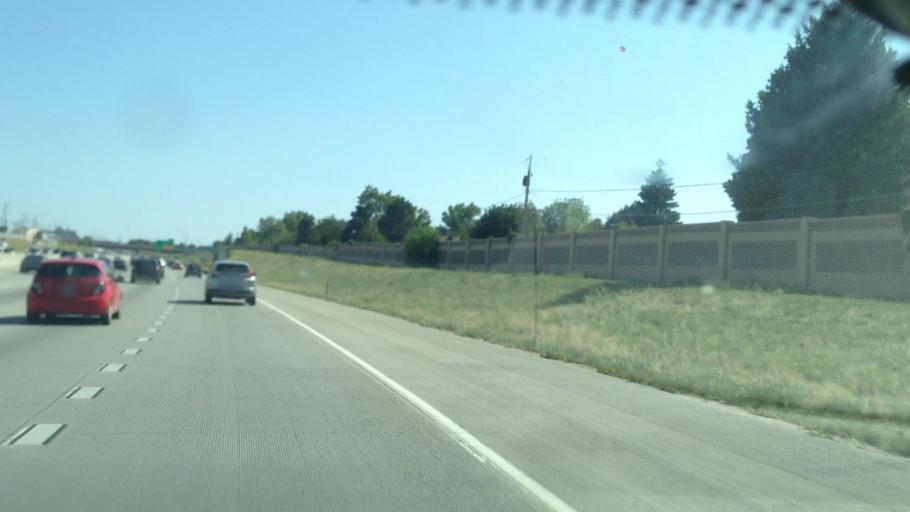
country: US
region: Colorado
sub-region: Adams County
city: Aurora
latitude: 39.7043
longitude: -104.8291
